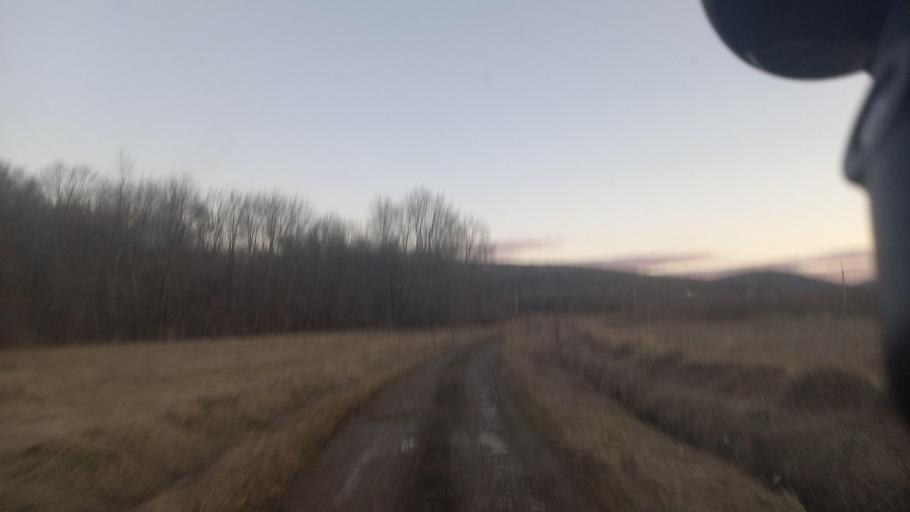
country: RU
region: Krasnodarskiy
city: Smolenskaya
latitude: 44.7298
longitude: 38.8374
